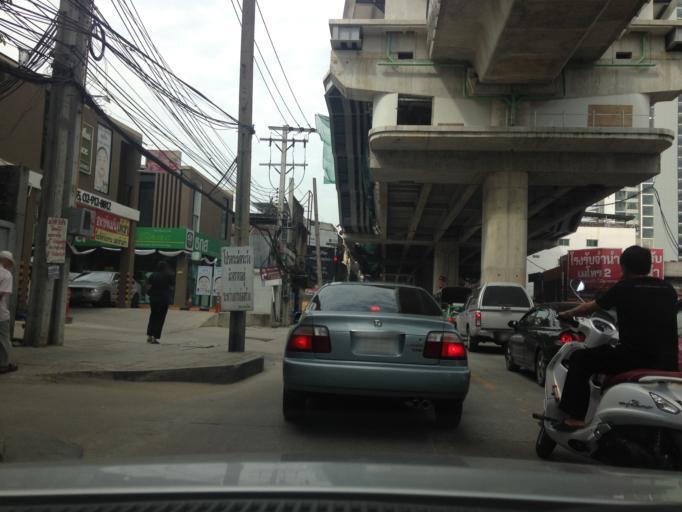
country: TH
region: Bangkok
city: Bang Sue
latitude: 13.8064
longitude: 100.5221
